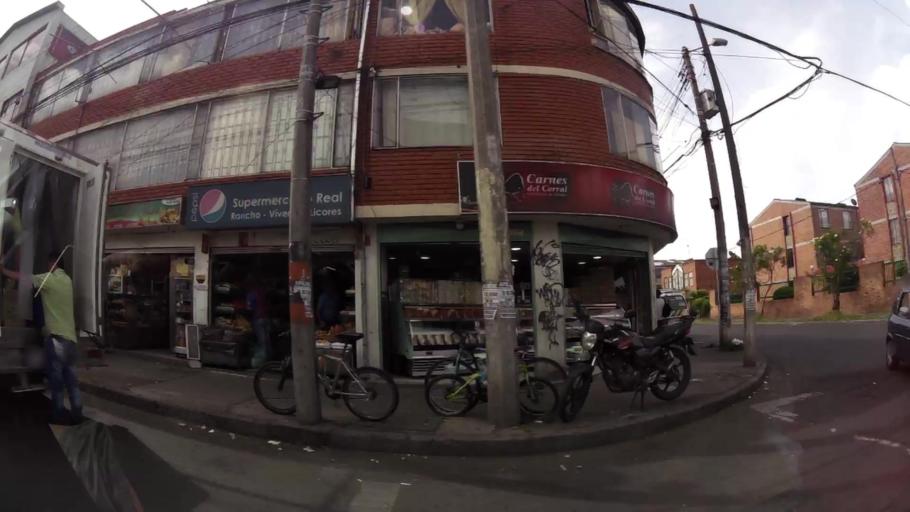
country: CO
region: Bogota D.C.
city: Bogota
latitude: 4.6438
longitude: -74.1392
